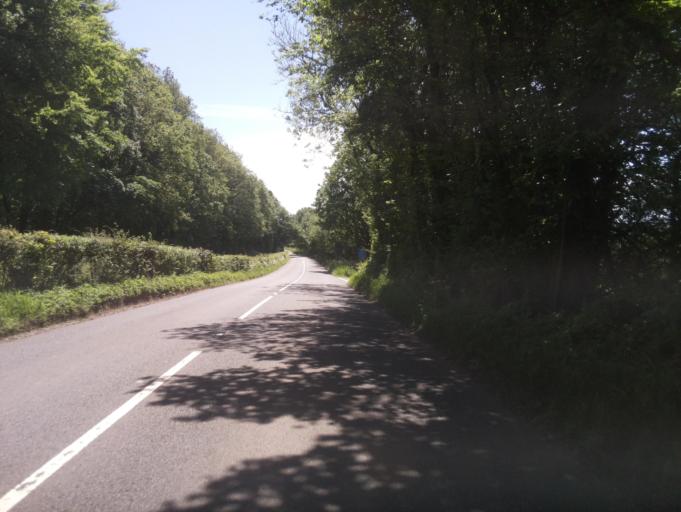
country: GB
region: Wales
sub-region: Monmouthshire
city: Tintern
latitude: 51.6794
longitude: -2.7527
